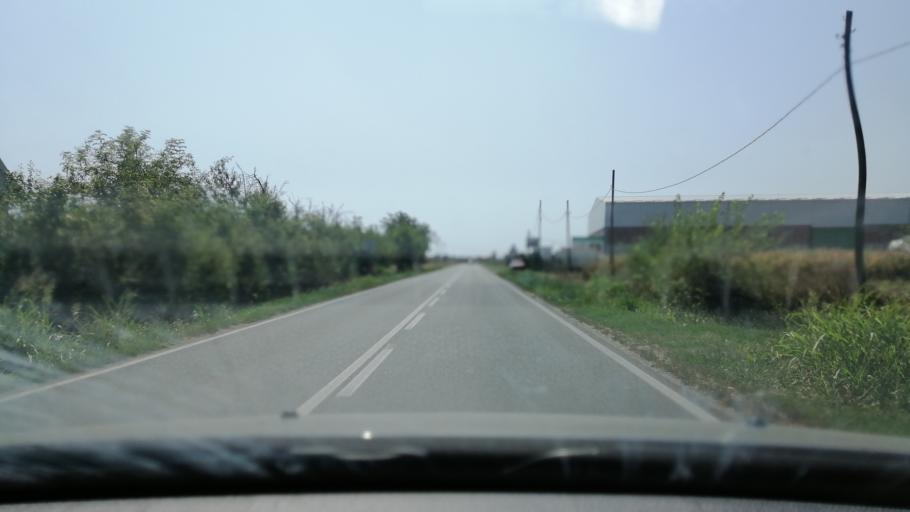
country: RS
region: Autonomna Pokrajina Vojvodina
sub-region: Juznobanatski Okrug
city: Pancevo
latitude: 44.7957
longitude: 20.7197
